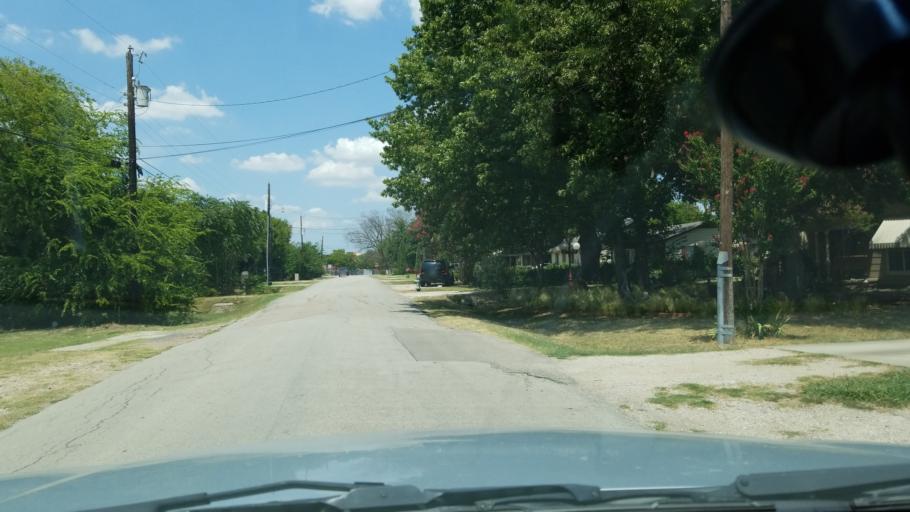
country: US
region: Texas
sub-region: Dallas County
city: Irving
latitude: 32.8295
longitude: -96.9923
